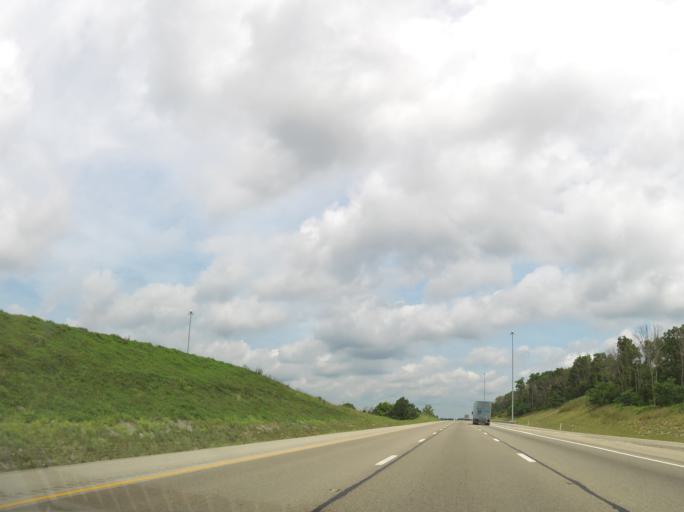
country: US
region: Kentucky
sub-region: Grant County
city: Williamstown
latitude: 38.4919
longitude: -84.5866
